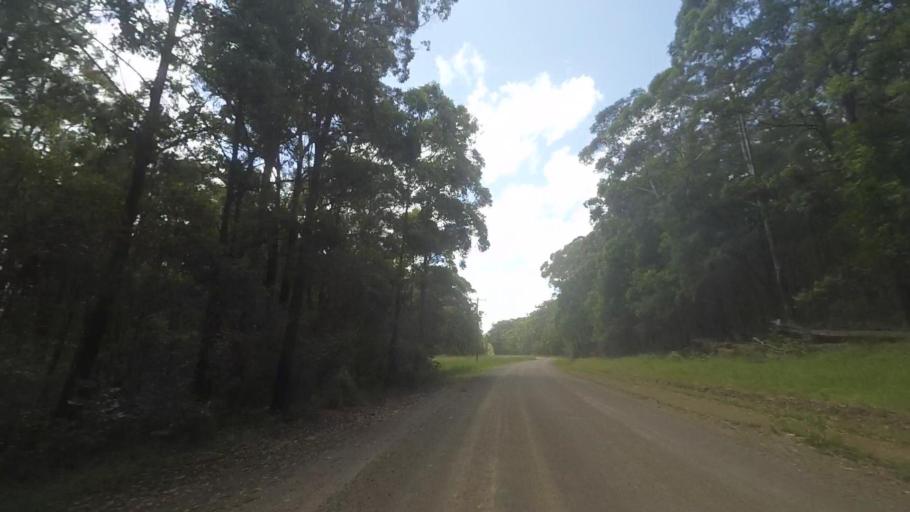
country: AU
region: New South Wales
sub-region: Great Lakes
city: Bulahdelah
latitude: -32.4981
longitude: 152.2789
